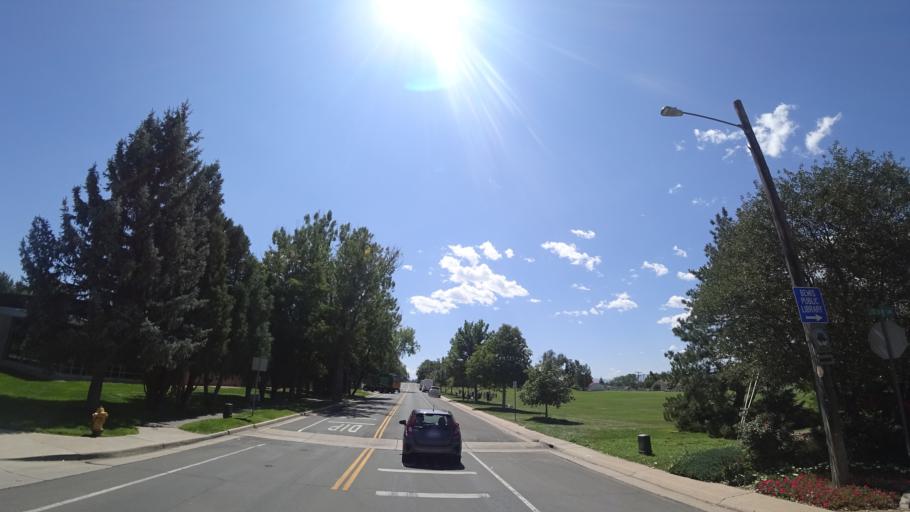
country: US
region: Colorado
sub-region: Arapahoe County
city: Littleton
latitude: 39.6070
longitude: -105.0021
